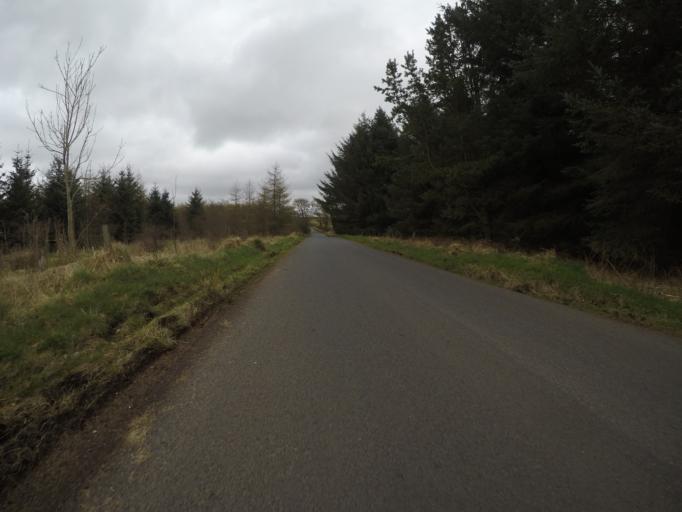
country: GB
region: Scotland
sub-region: East Ayrshire
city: Stewarton
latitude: 55.6804
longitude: -4.4525
